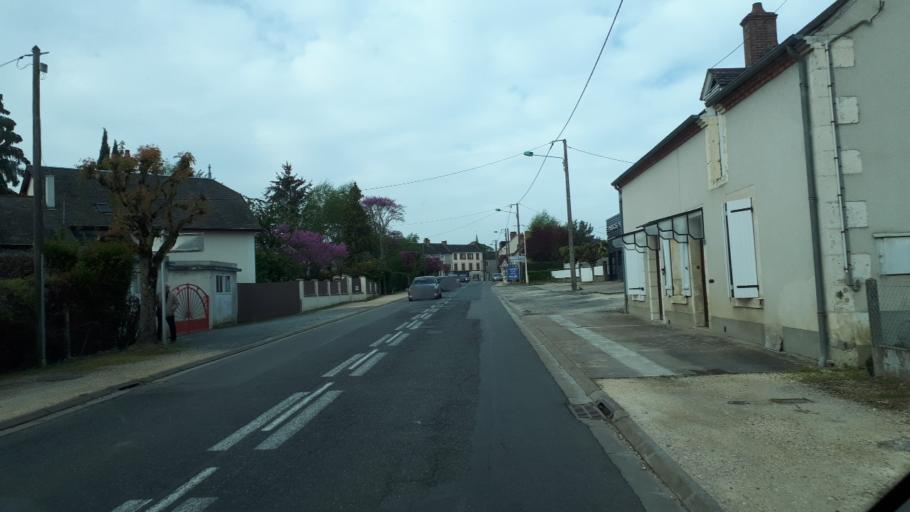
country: FR
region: Centre
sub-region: Departement du Cher
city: Rians
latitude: 47.2005
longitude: 2.5767
